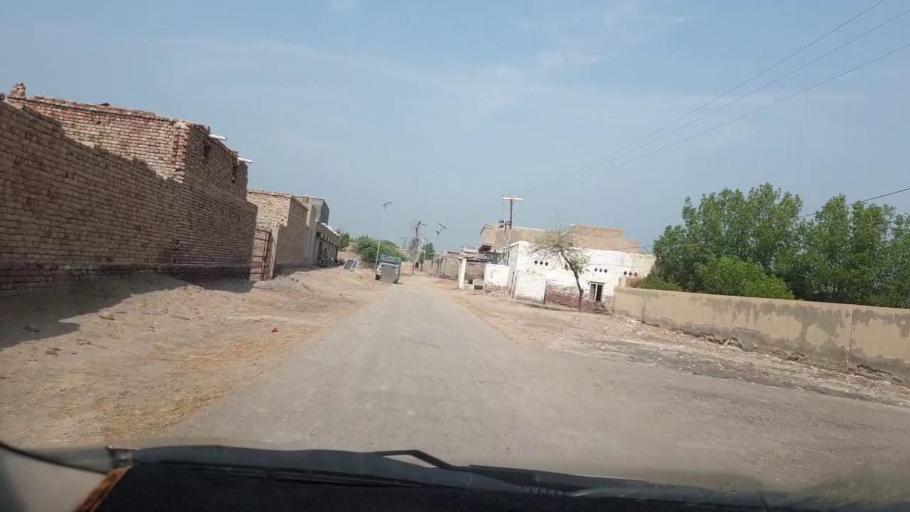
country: PK
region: Sindh
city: Goth Garelo
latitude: 27.4843
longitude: 68.0397
